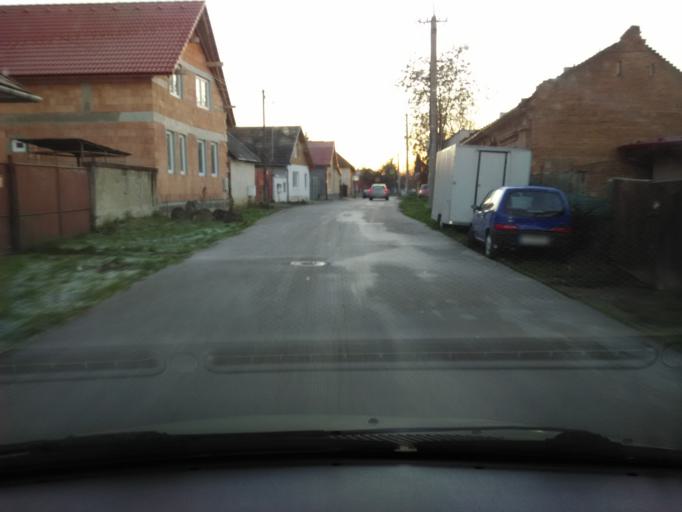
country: SK
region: Nitriansky
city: Levice
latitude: 48.2257
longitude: 18.6051
